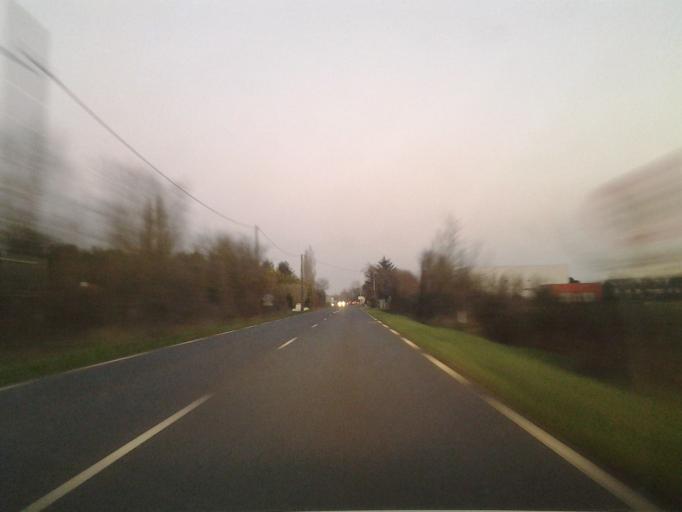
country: FR
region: Pays de la Loire
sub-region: Departement de la Vendee
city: Sallertaine
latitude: 46.8711
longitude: -1.9394
